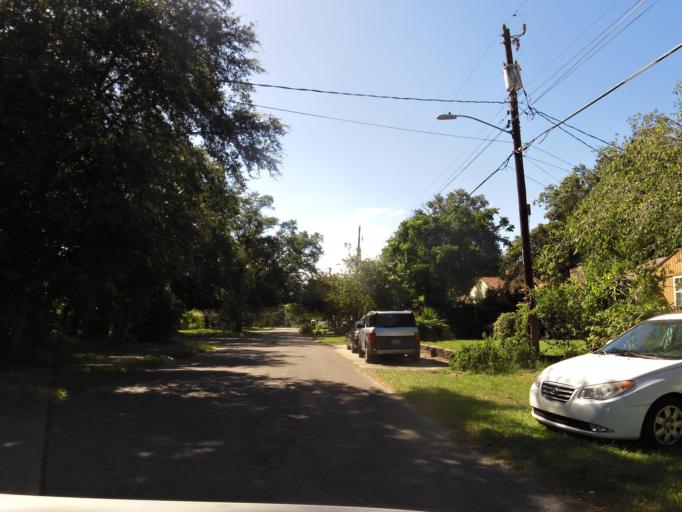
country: US
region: Florida
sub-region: Duval County
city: Jacksonville
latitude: 30.2719
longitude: -81.7267
